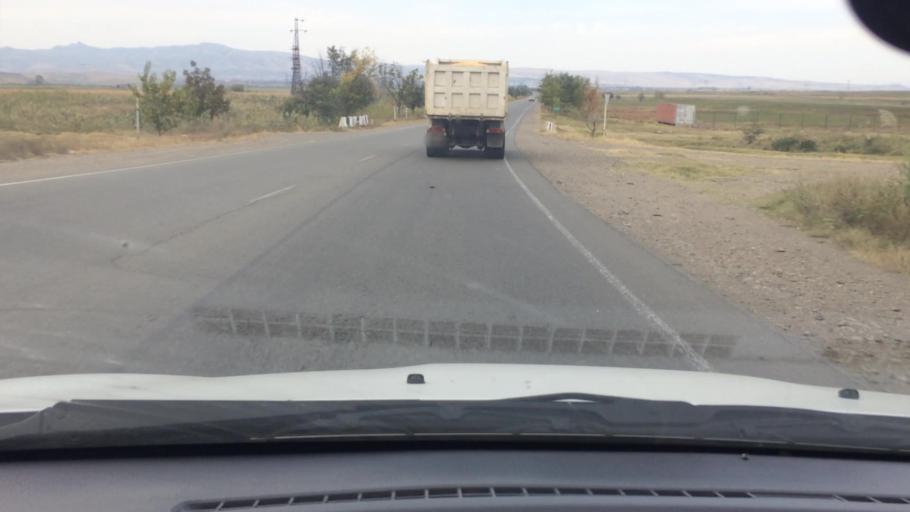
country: GE
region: Kvemo Kartli
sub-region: Marneuli
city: Marneuli
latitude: 41.5261
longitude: 44.7772
